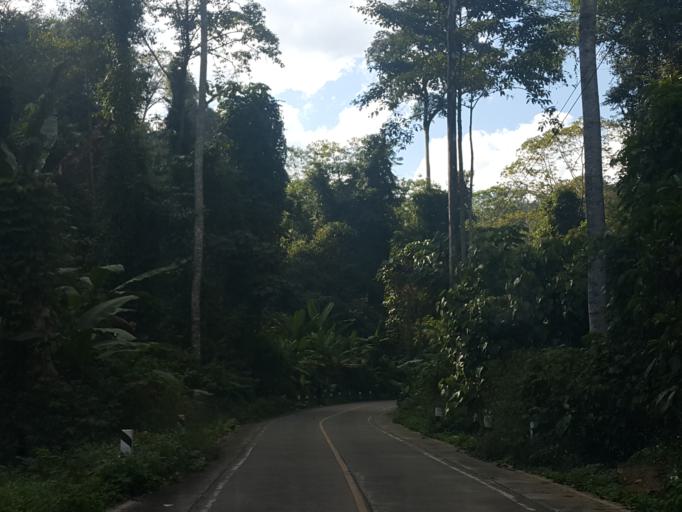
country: TH
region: Chiang Mai
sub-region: Amphoe Chiang Dao
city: Chiang Dao
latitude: 19.4134
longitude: 98.9171
